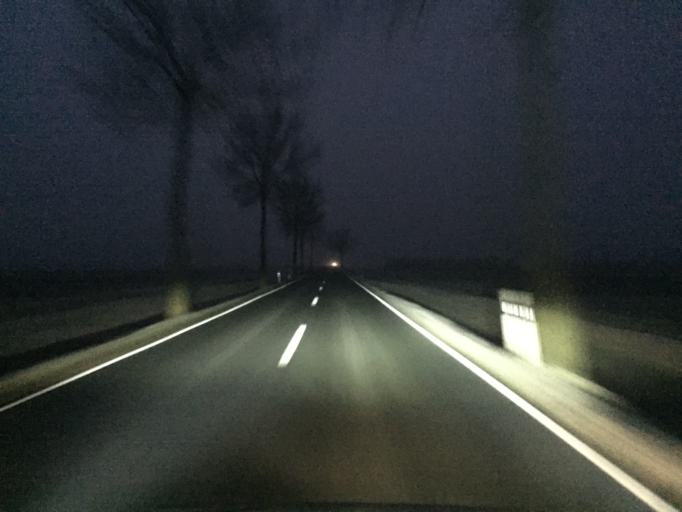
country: DE
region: Lower Saxony
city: Maasen
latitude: 52.6627
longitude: 8.8883
